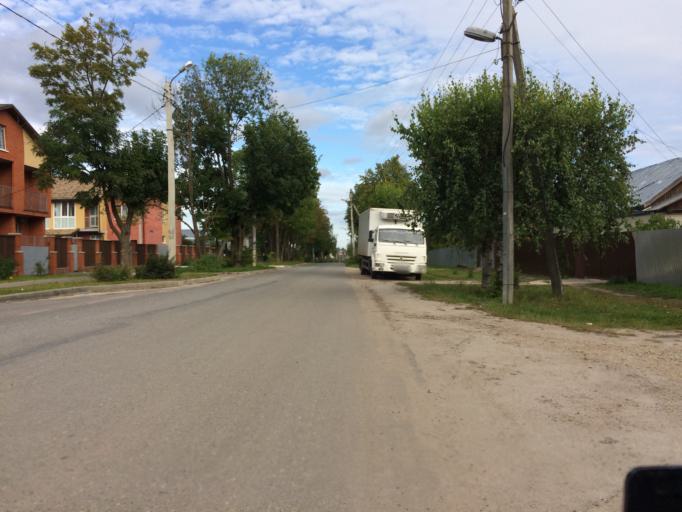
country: RU
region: Mariy-El
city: Yoshkar-Ola
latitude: 56.6505
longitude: 47.9730
